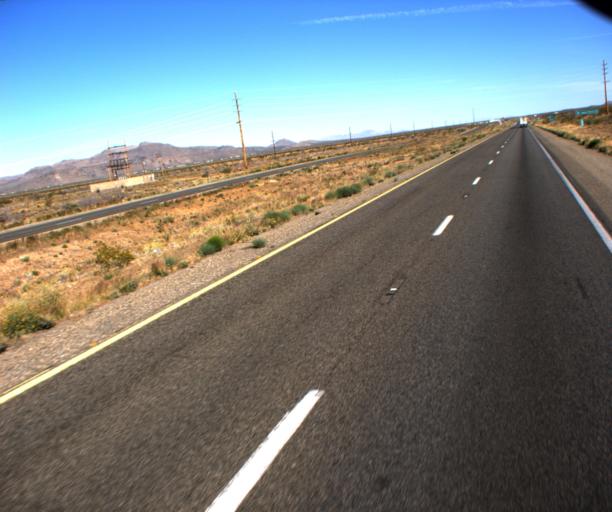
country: US
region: Arizona
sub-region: Mohave County
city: Golden Valley
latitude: 35.3182
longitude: -114.2022
